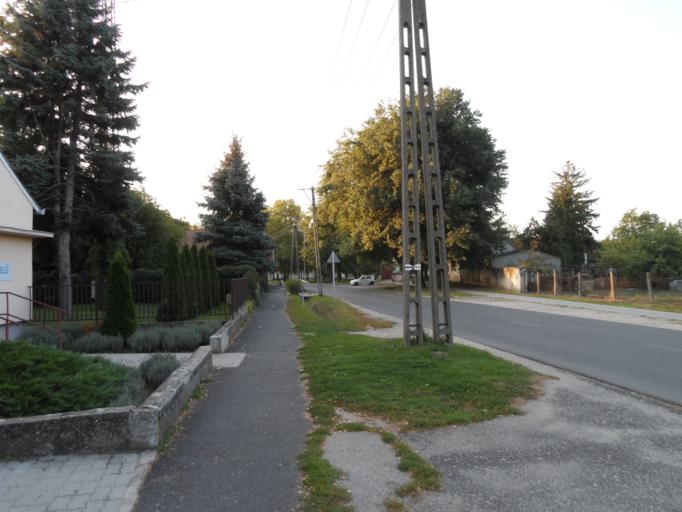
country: HU
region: Veszprem
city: Devecser
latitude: 47.1214
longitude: 17.3765
